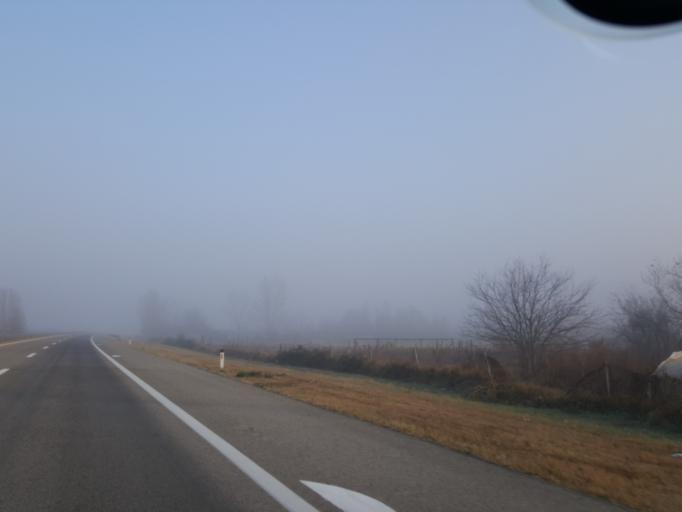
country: RS
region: Central Serbia
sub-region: Jablanicki Okrug
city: Leskovac
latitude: 42.9955
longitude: 22.0257
